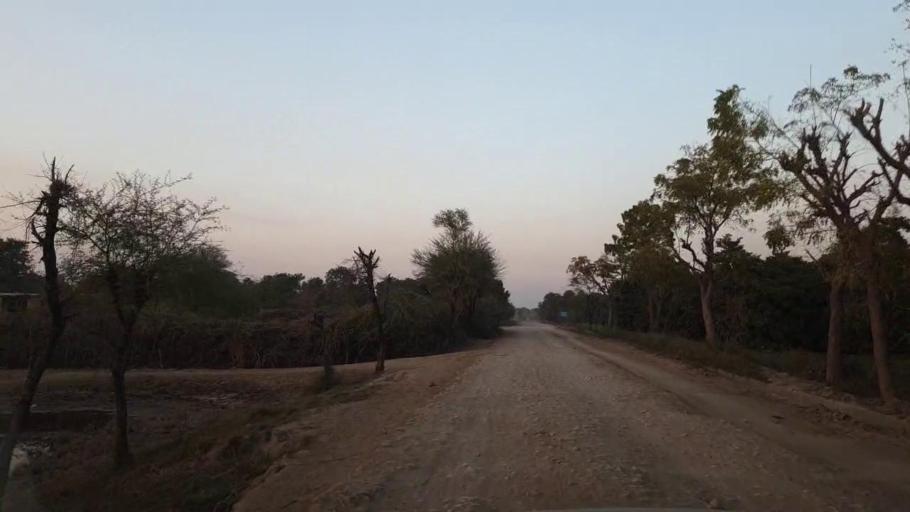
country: PK
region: Sindh
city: Berani
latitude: 25.6624
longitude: 68.7884
